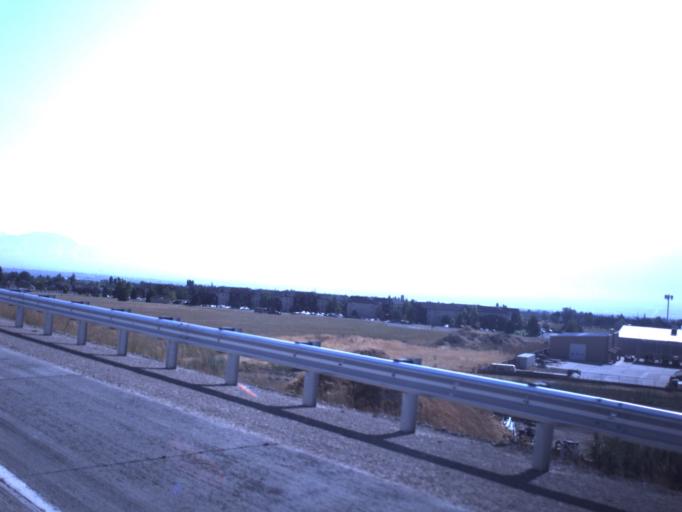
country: US
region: Utah
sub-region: Salt Lake County
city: Oquirrh
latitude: 40.5843
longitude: -112.0287
